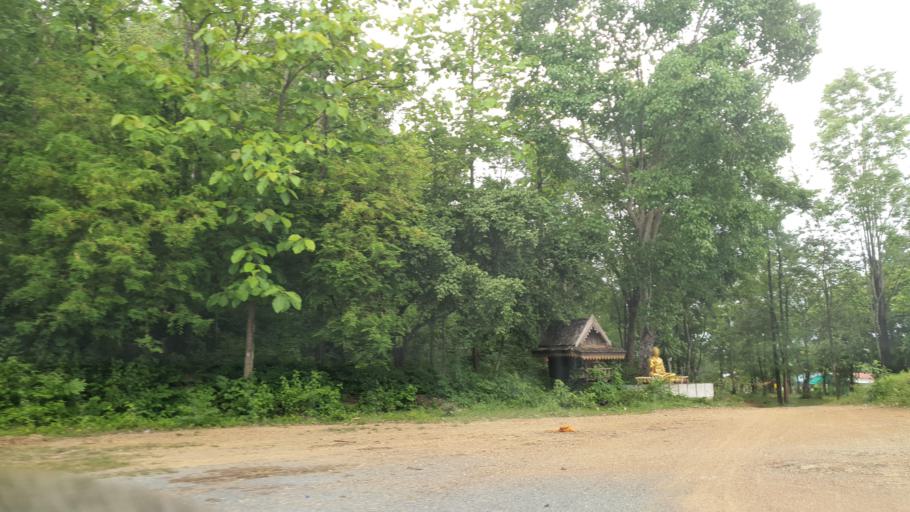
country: TH
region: Sukhothai
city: Thung Saliam
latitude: 17.2639
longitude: 99.5362
